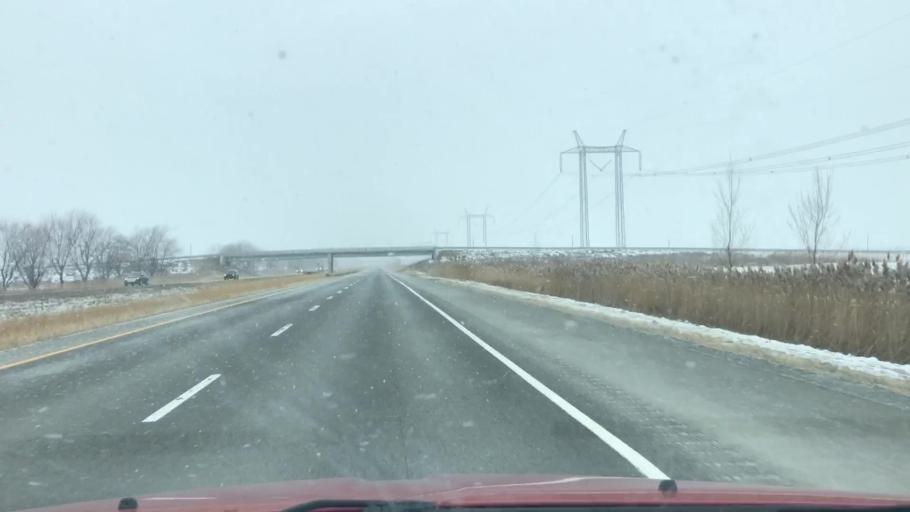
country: CA
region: Quebec
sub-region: Monteregie
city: Rougemont
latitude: 45.3791
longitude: -73.0536
